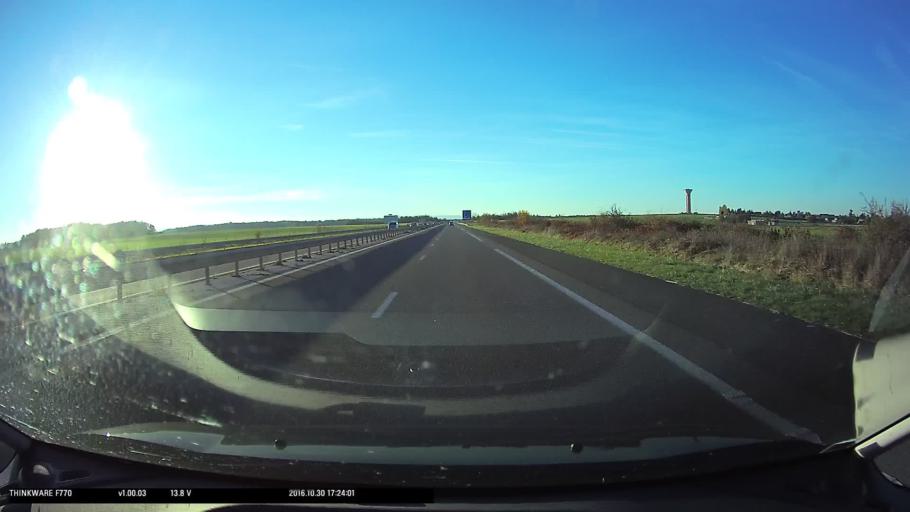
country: FR
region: Bourgogne
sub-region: Departement de la Cote-d'Or
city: Genlis
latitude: 47.2676
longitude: 5.1809
